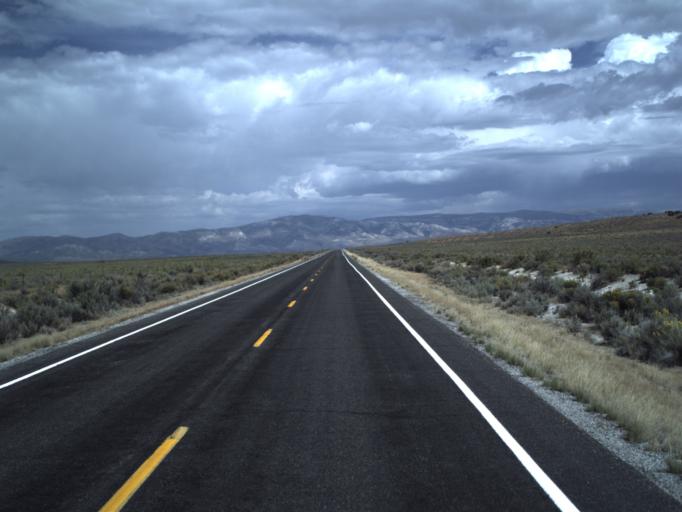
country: US
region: Idaho
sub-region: Cassia County
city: Burley
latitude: 41.6720
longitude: -113.5438
